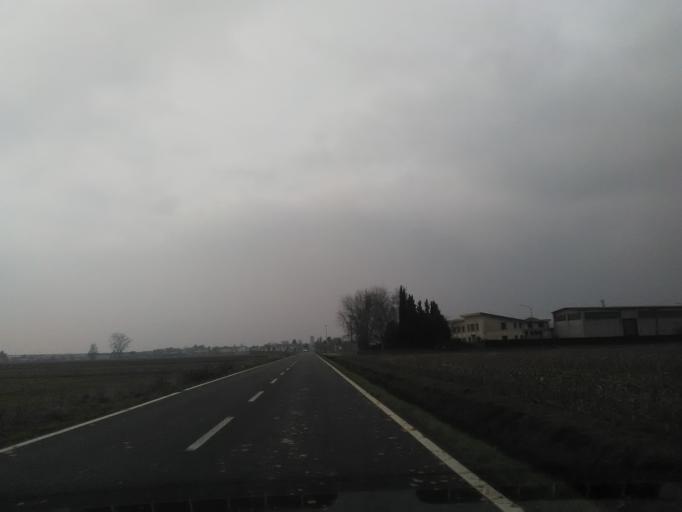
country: IT
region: Piedmont
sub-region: Provincia di Vercelli
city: Bianze
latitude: 45.3158
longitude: 8.1312
